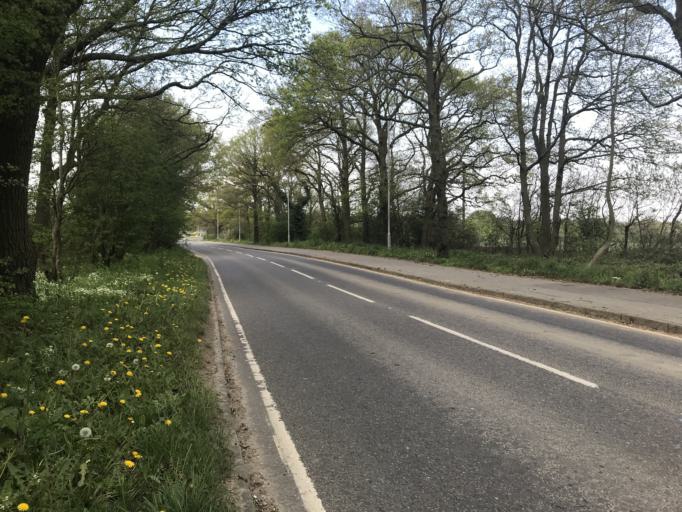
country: GB
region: England
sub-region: Essex
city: Stock
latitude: 51.6848
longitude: 0.4661
